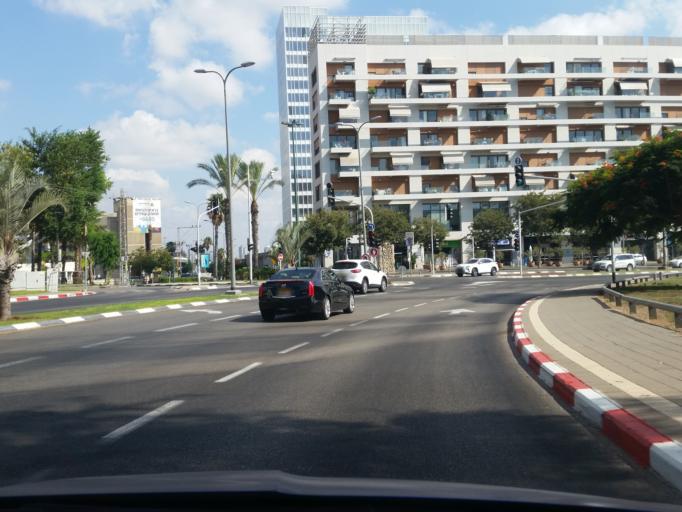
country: IL
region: Tel Aviv
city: Ramat HaSharon
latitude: 32.1149
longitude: 34.8402
